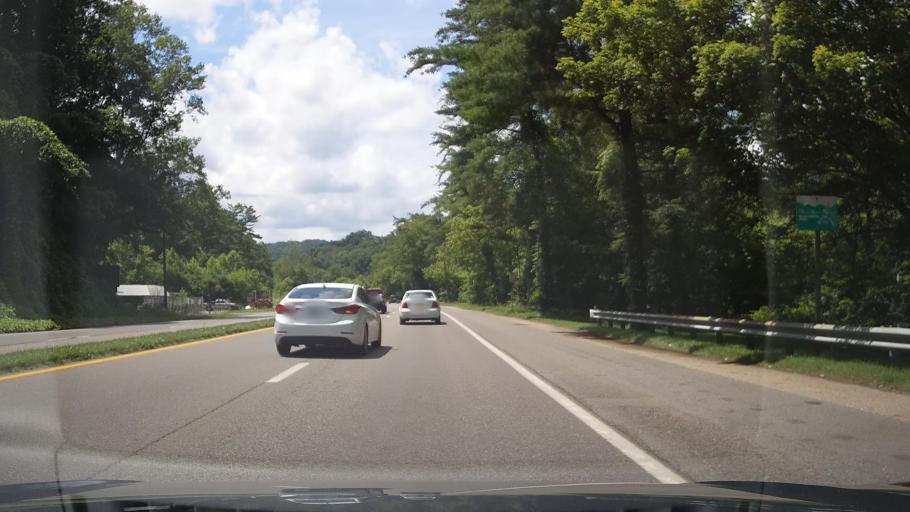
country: US
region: Virginia
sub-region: Scott County
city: Weber City
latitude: 36.6359
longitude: -82.5527
